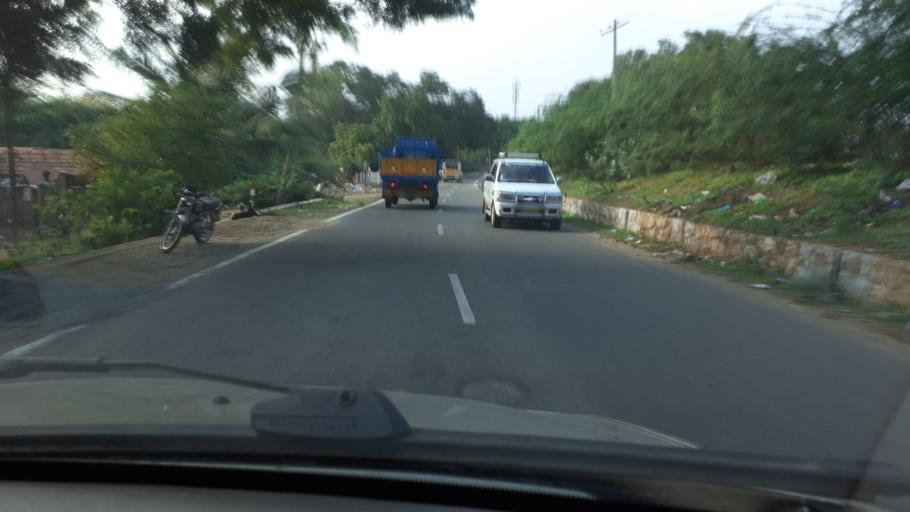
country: IN
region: Tamil Nadu
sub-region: Thoothukkudi
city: Srivaikuntam
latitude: 8.6207
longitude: 77.9111
